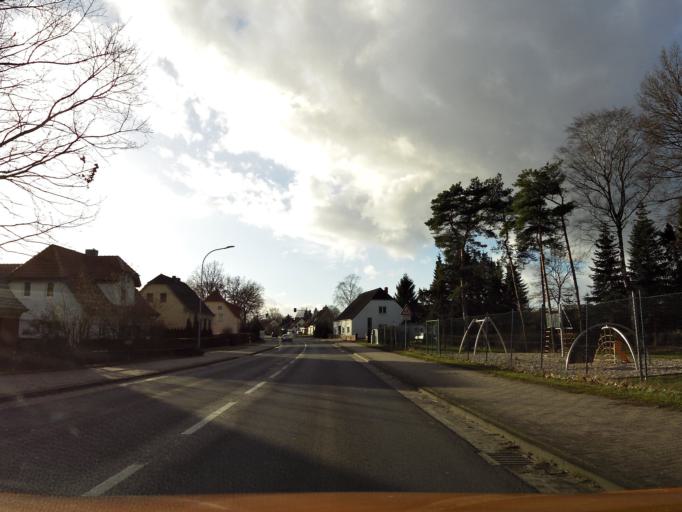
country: DE
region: Lower Saxony
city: Langwedel
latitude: 52.9814
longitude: 9.1764
